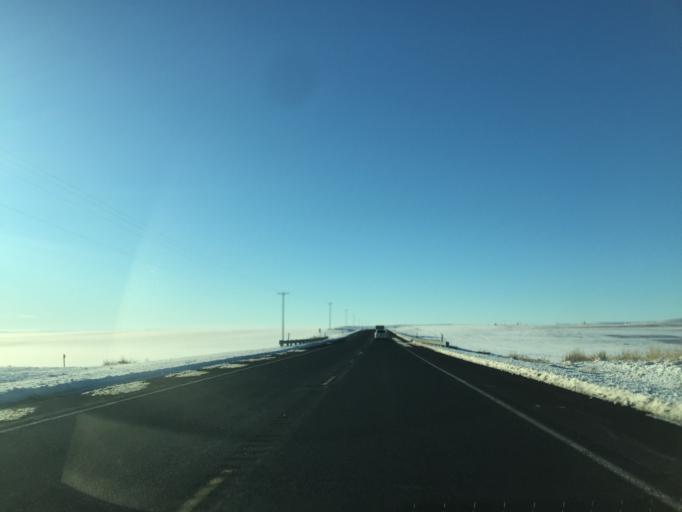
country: US
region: Washington
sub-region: Okanogan County
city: Coulee Dam
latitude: 47.6846
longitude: -119.0747
